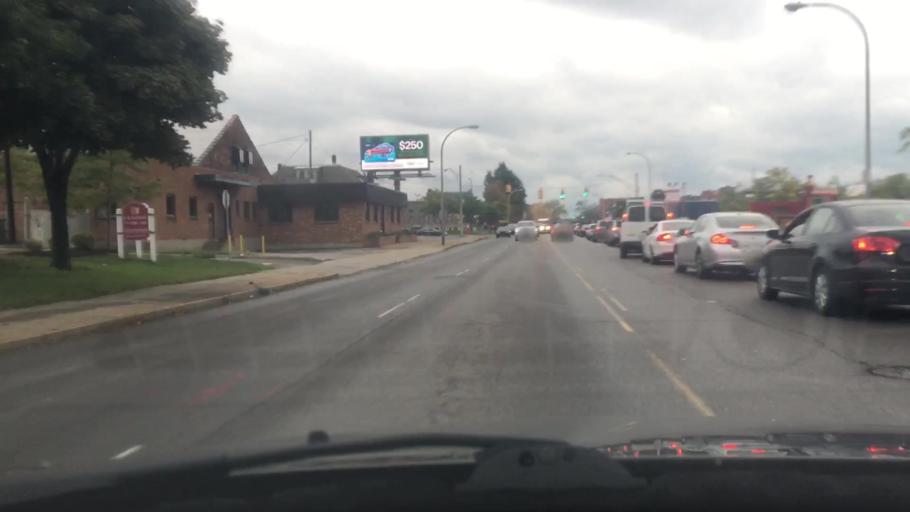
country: US
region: New York
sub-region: Erie County
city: Kenmore
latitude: 42.9489
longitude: -78.8783
